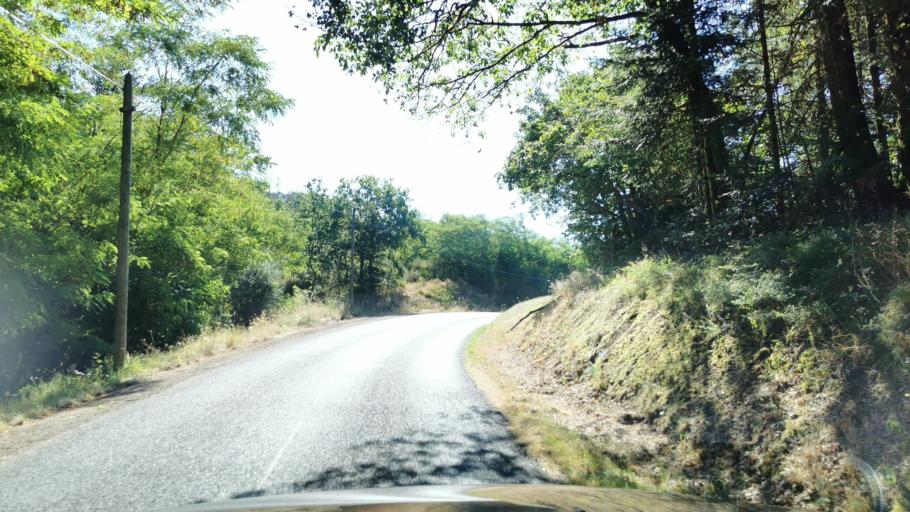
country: FR
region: Bourgogne
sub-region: Departement de Saone-et-Loire
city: Montcenis
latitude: 46.7941
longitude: 4.3732
